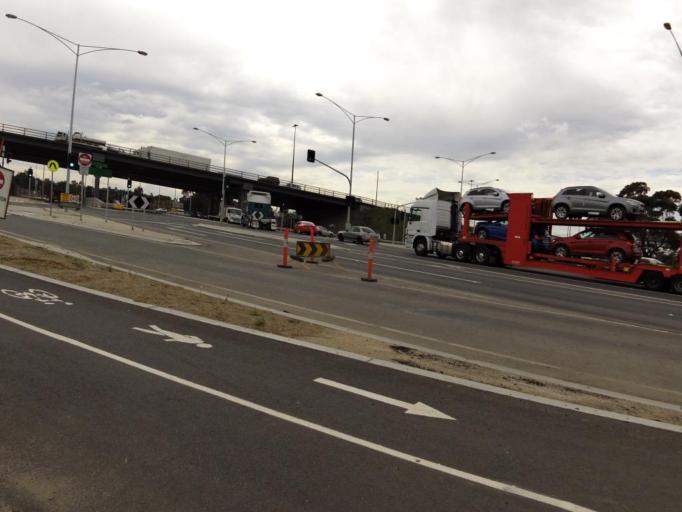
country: AU
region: Victoria
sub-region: Maribyrnong
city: Yarraville
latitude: -37.8342
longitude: 144.9129
